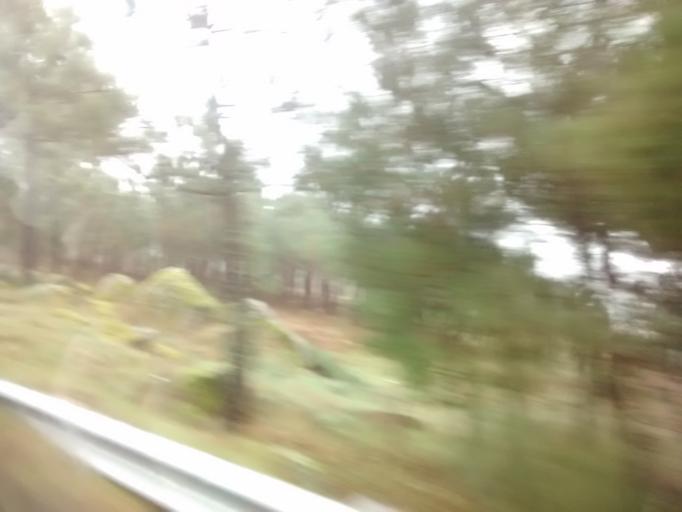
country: PT
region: Guarda
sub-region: Seia
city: Seia
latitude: 40.4149
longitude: -7.6793
